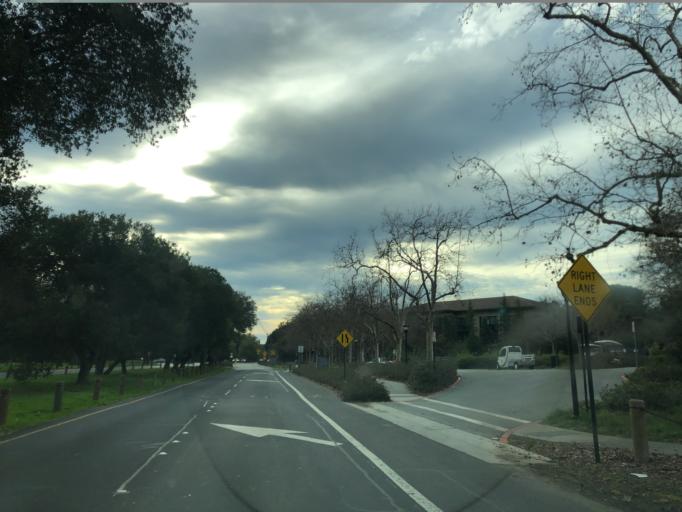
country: US
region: California
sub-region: Santa Clara County
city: Stanford
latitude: 37.4328
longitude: -122.1657
